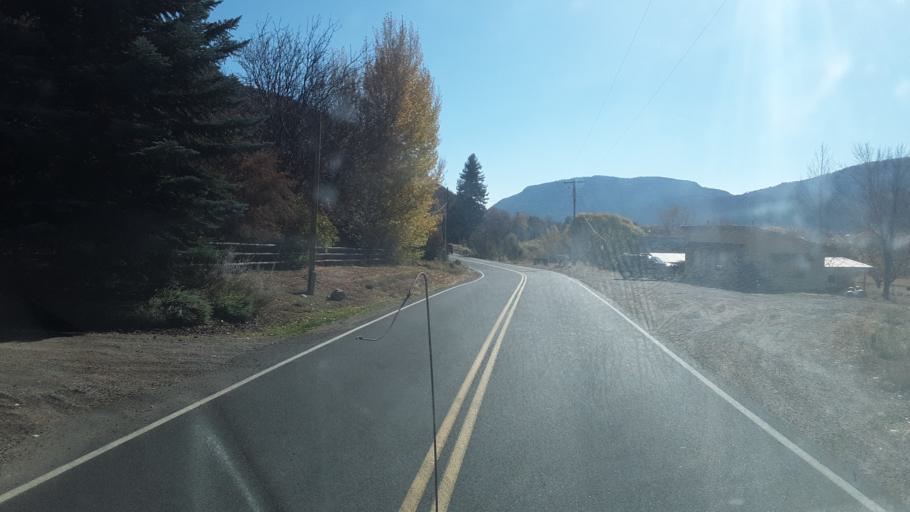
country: US
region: Colorado
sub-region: La Plata County
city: Durango
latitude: 37.3825
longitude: -107.8350
